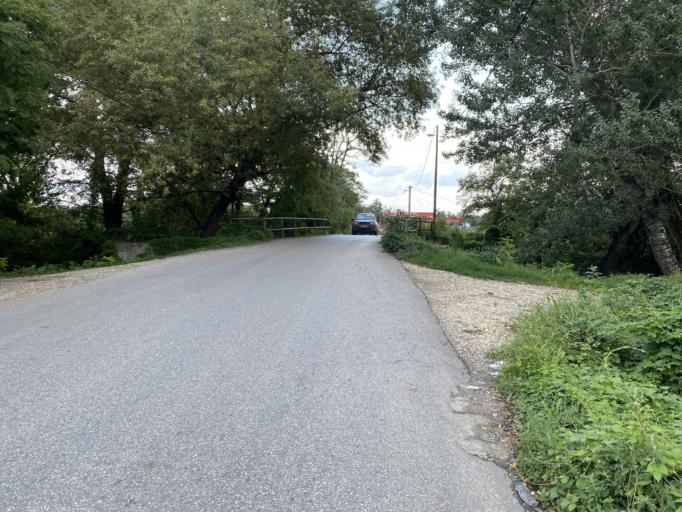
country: MK
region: Kisela Voda
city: Kisela Voda
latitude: 41.9642
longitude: 21.4997
